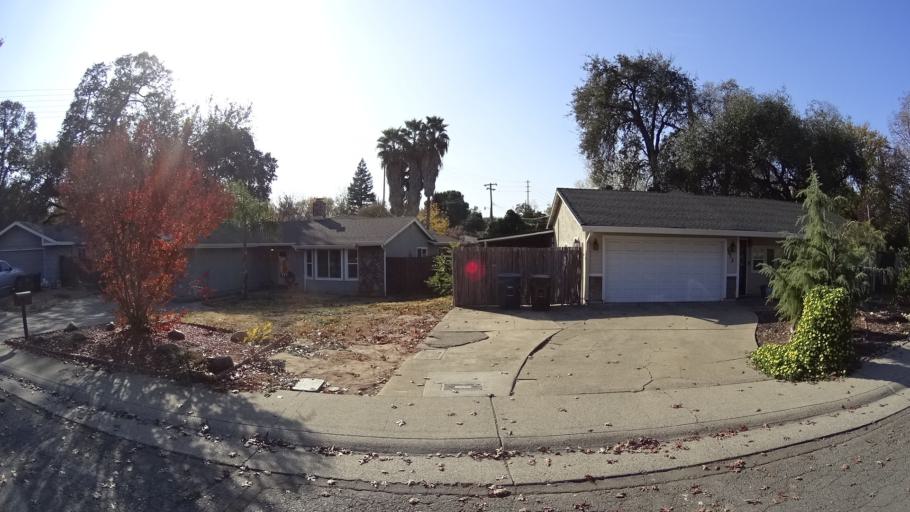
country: US
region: California
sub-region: Sacramento County
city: Citrus Heights
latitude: 38.6862
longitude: -121.2784
